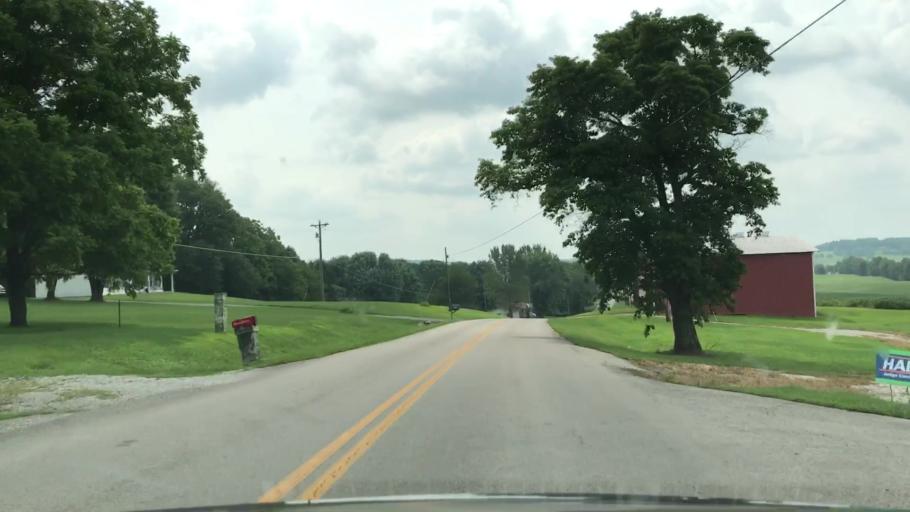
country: US
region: Kentucky
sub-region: Barren County
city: Cave City
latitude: 37.1068
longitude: -85.9811
